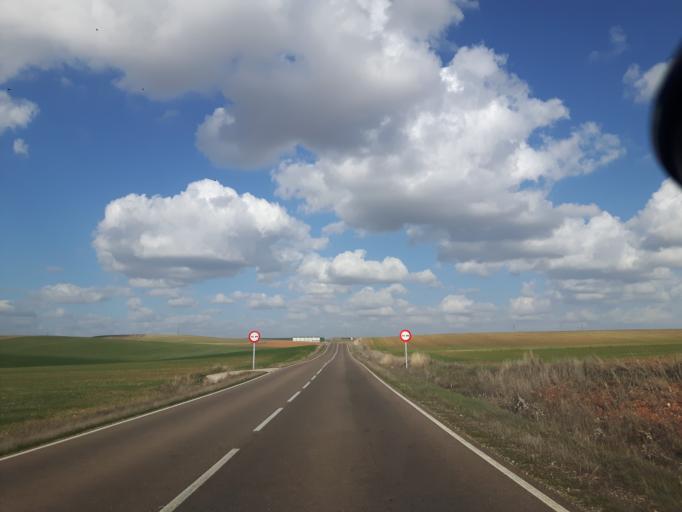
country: ES
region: Castille and Leon
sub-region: Provincia de Salamanca
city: Cabrerizos
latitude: 40.9884
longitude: -5.6002
